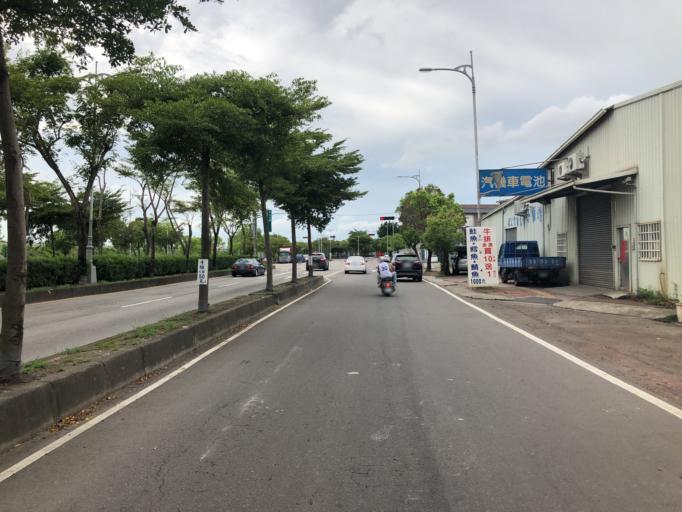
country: TW
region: Taiwan
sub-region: Taichung City
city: Taichung
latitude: 24.0894
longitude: 120.6541
